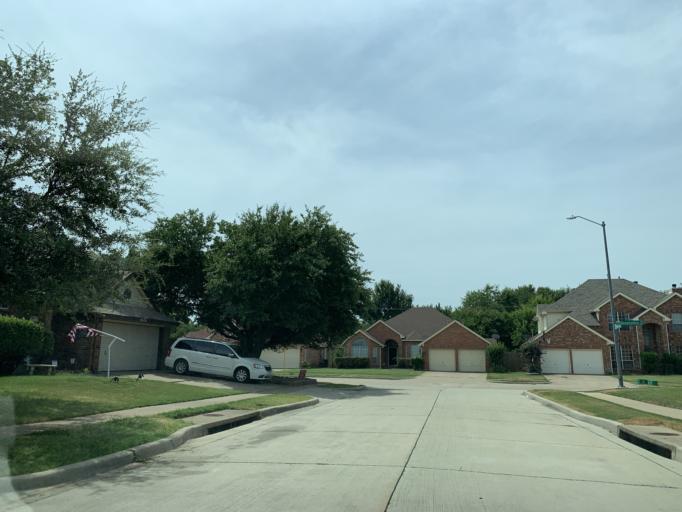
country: US
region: Texas
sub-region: Dallas County
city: Cedar Hill
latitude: 32.6557
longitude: -97.0081
